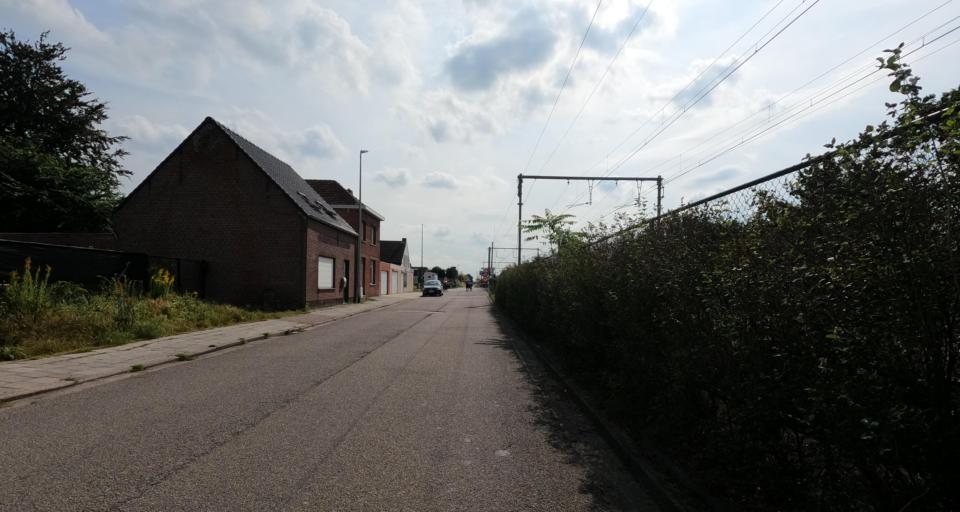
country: BE
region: Flanders
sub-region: Provincie Antwerpen
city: Essen
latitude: 51.4559
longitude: 4.4537
